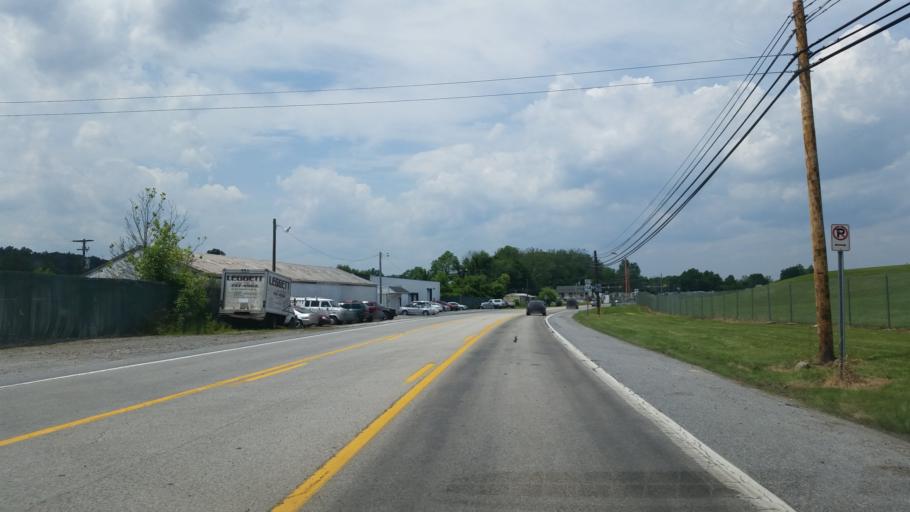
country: US
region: Pennsylvania
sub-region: Dauphin County
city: Steelton
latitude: 40.2142
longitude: -76.8593
